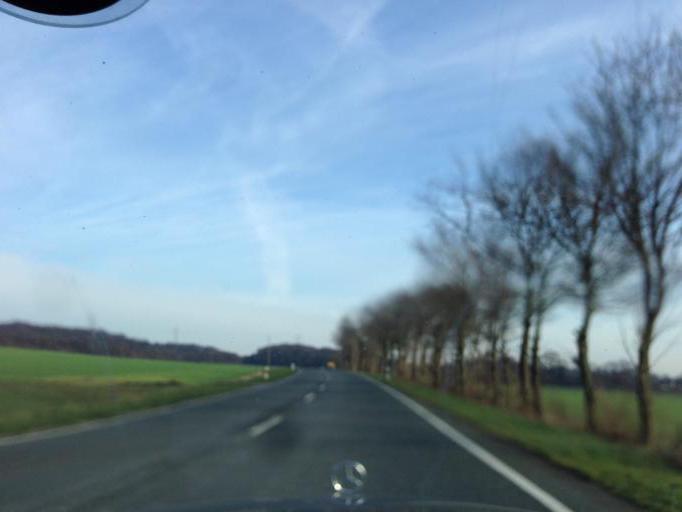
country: DE
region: North Rhine-Westphalia
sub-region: Regierungsbezirk Munster
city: Tecklenburg
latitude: 52.2495
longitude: 7.7913
